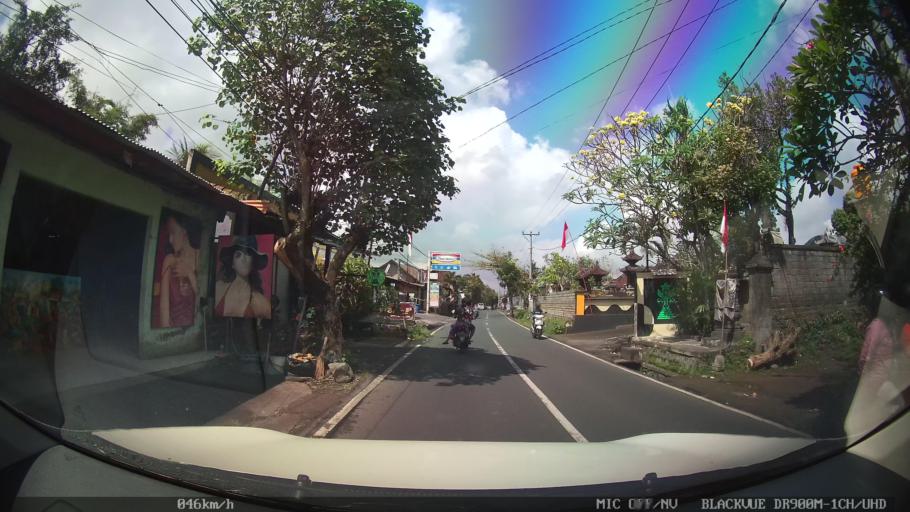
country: ID
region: Bali
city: Banjar Sedang
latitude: -8.5662
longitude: 115.2620
